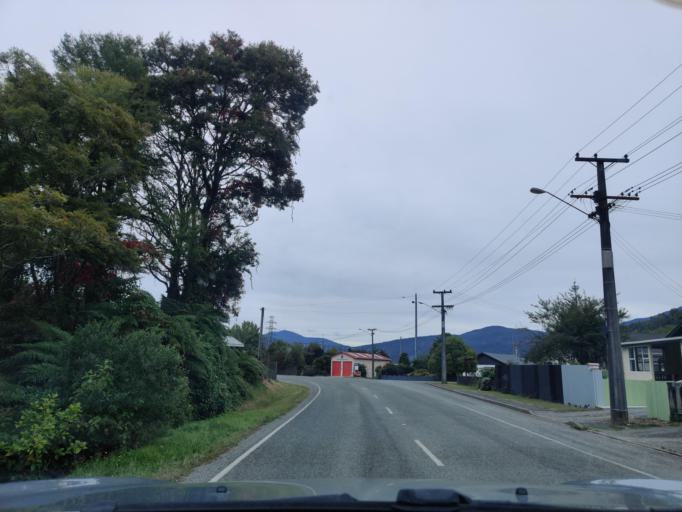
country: NZ
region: West Coast
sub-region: Buller District
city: Westport
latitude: -41.8577
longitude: 171.9514
